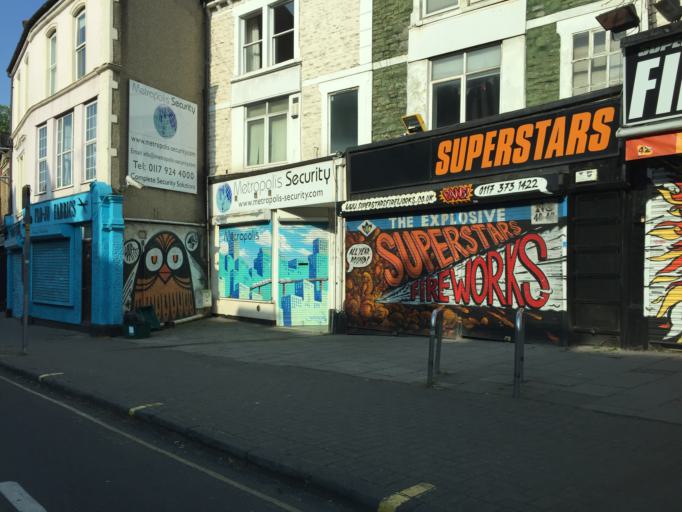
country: GB
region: England
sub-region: Bristol
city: Bristol
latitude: 51.4728
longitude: -2.5912
